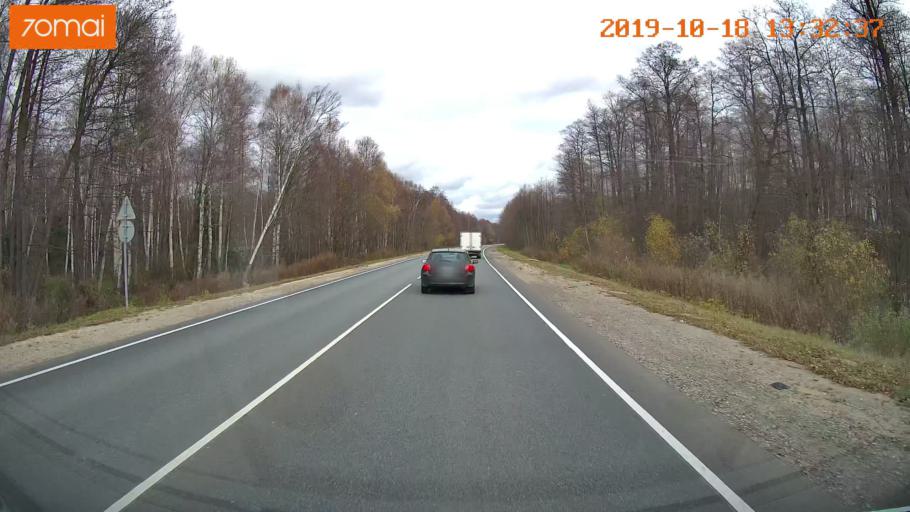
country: RU
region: Rjazan
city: Solotcha
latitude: 54.8352
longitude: 39.9210
